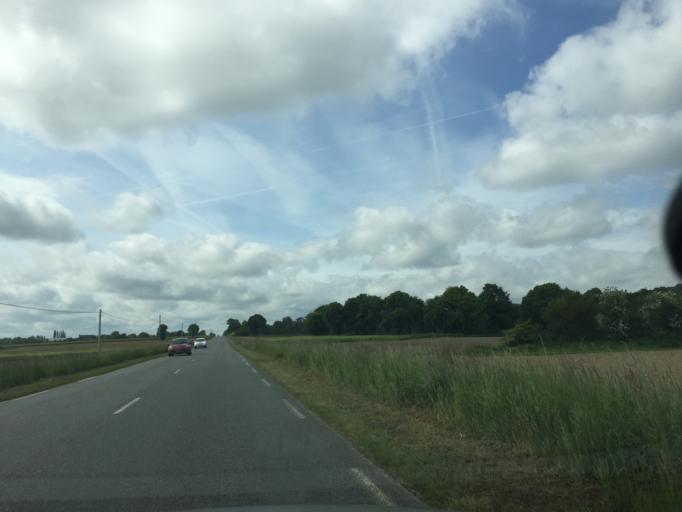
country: FR
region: Brittany
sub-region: Departement des Cotes-d'Armor
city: Crehen
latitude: 48.5612
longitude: -2.1906
